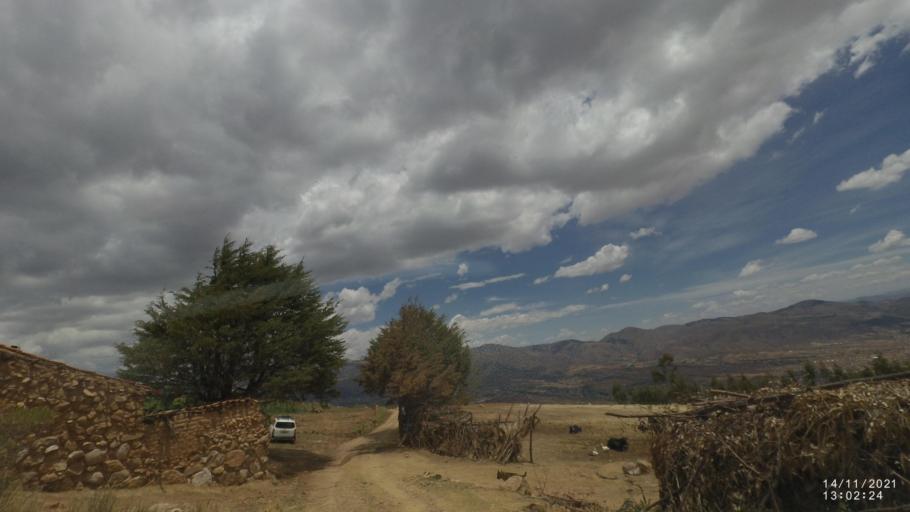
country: BO
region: Cochabamba
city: Colomi
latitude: -17.3686
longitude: -65.9768
